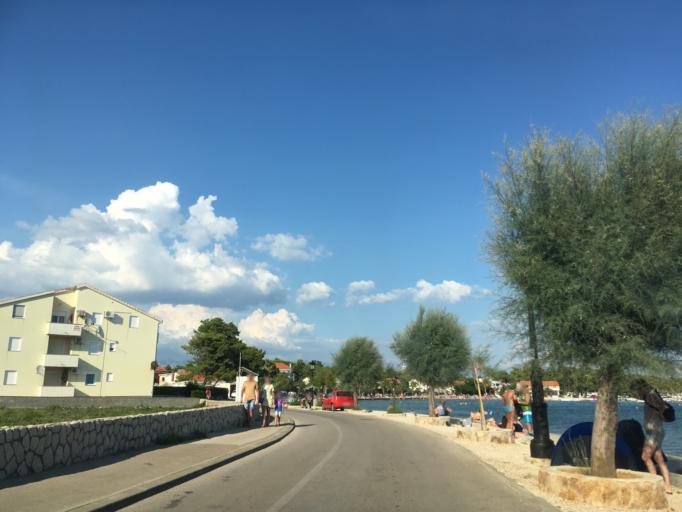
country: HR
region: Zadarska
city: Vir
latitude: 44.2977
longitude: 15.0928
